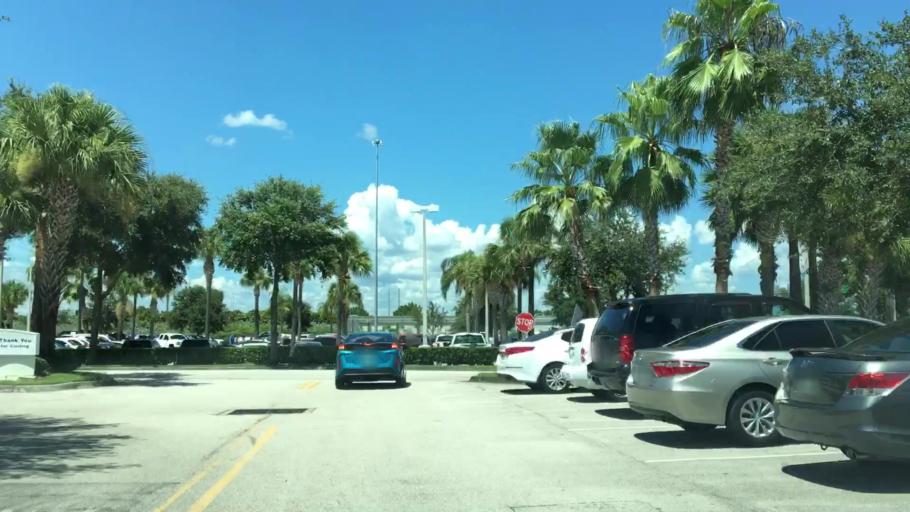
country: US
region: Florida
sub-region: Seminole County
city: Lake Mary
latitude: 28.7946
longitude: -81.3408
